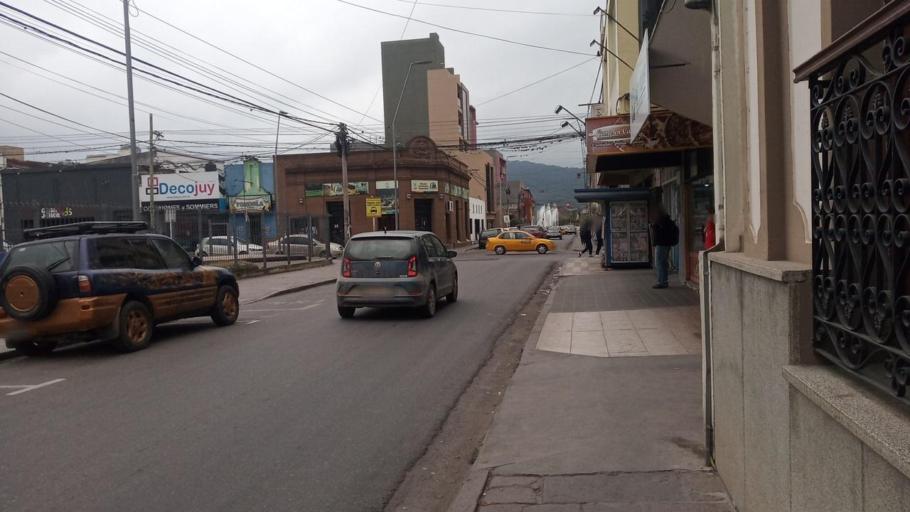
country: AR
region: Jujuy
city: San Salvador de Jujuy
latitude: -24.1844
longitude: -65.3017
